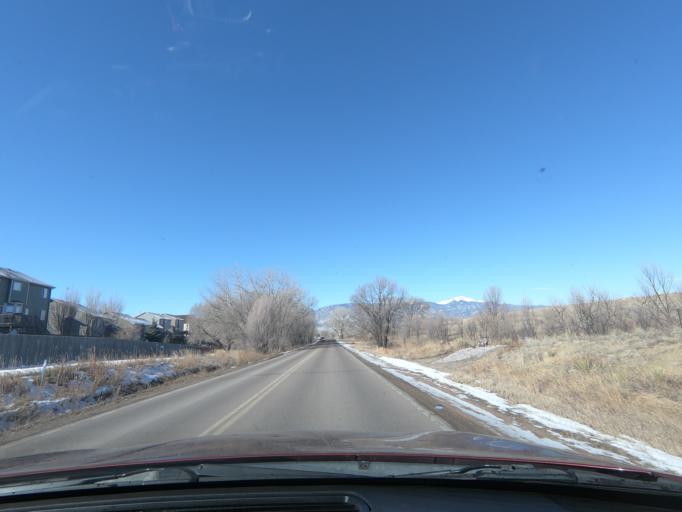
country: US
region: Colorado
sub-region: El Paso County
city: Security-Widefield
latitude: 38.7375
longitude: -104.6982
